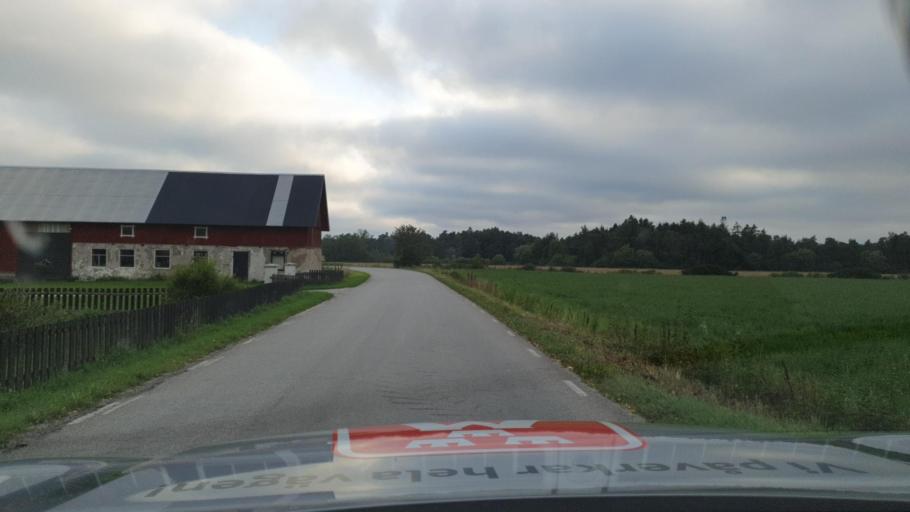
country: SE
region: Gotland
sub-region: Gotland
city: Vibble
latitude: 57.5041
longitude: 18.2032
